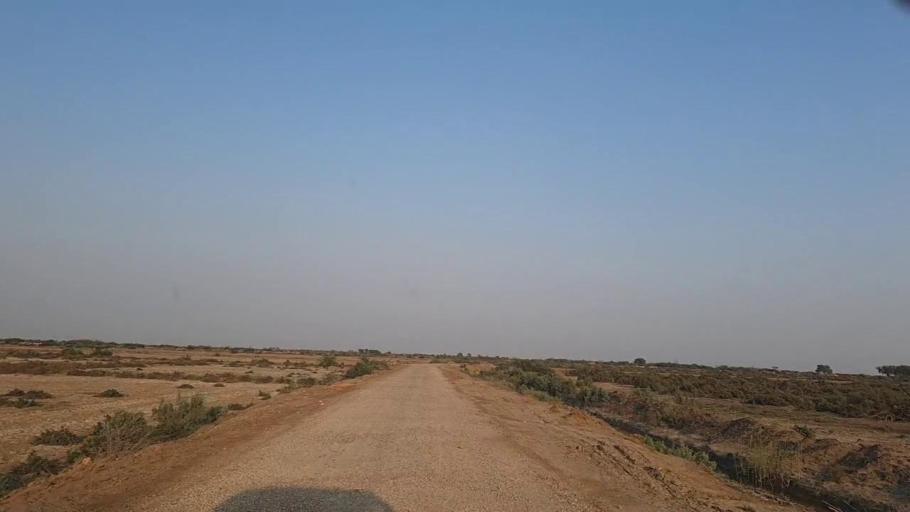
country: PK
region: Sindh
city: Jati
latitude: 24.4889
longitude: 68.4139
